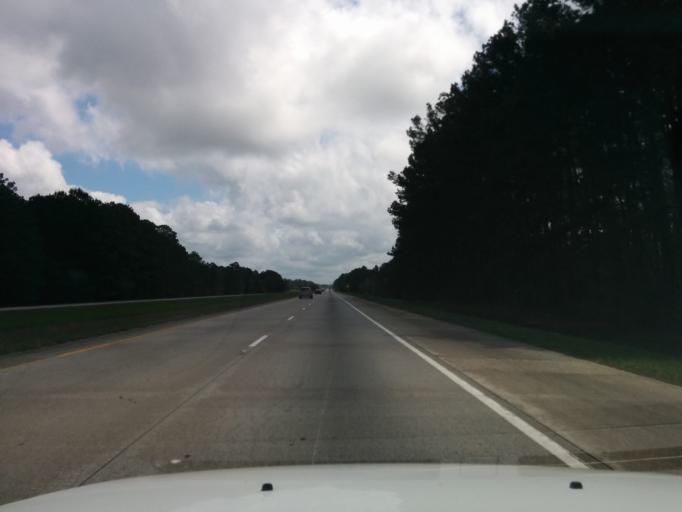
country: US
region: Georgia
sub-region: Bulloch County
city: Brooklet
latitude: 32.2738
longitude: -81.7533
